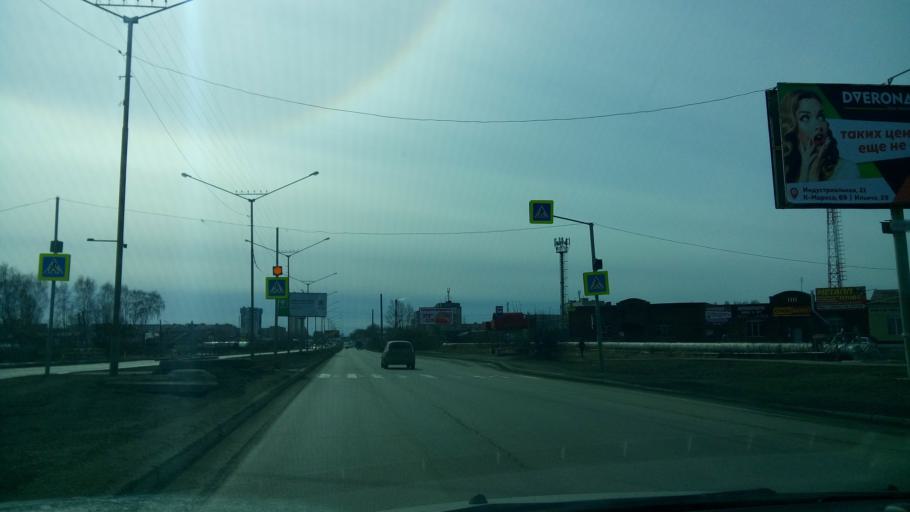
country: RU
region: Sverdlovsk
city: Nizhniy Tagil
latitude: 57.8938
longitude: 59.9409
